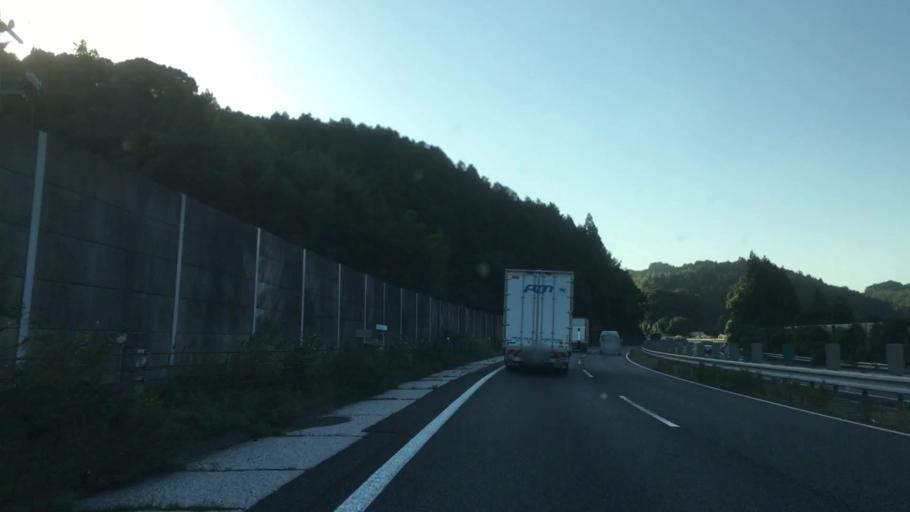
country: JP
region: Yamaguchi
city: Onoda
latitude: 34.1155
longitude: 131.1292
